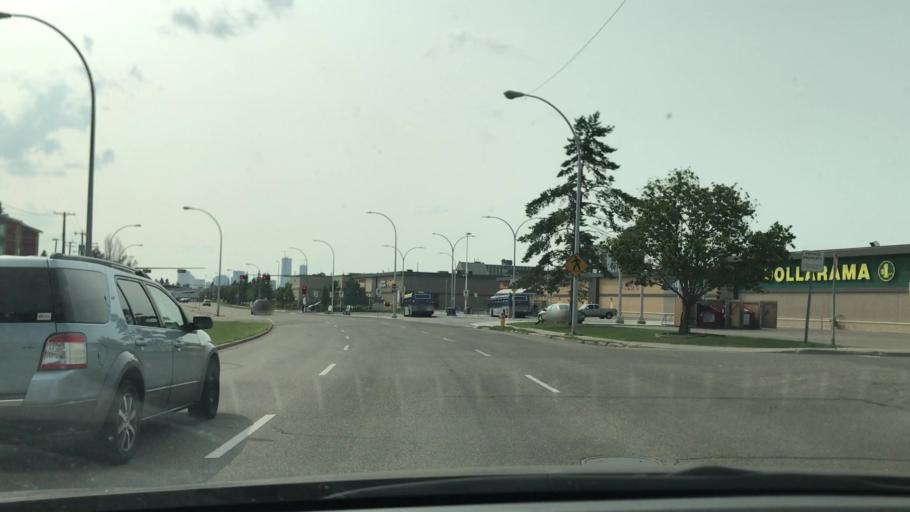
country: CA
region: Alberta
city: Edmonton
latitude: 53.5383
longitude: -113.4213
